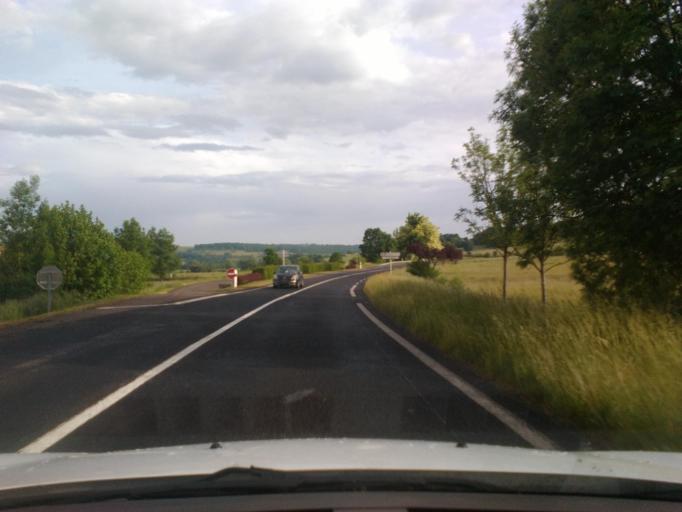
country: FR
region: Lorraine
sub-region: Departement de Meurthe-et-Moselle
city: Gerbeviller
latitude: 48.4506
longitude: 6.5629
